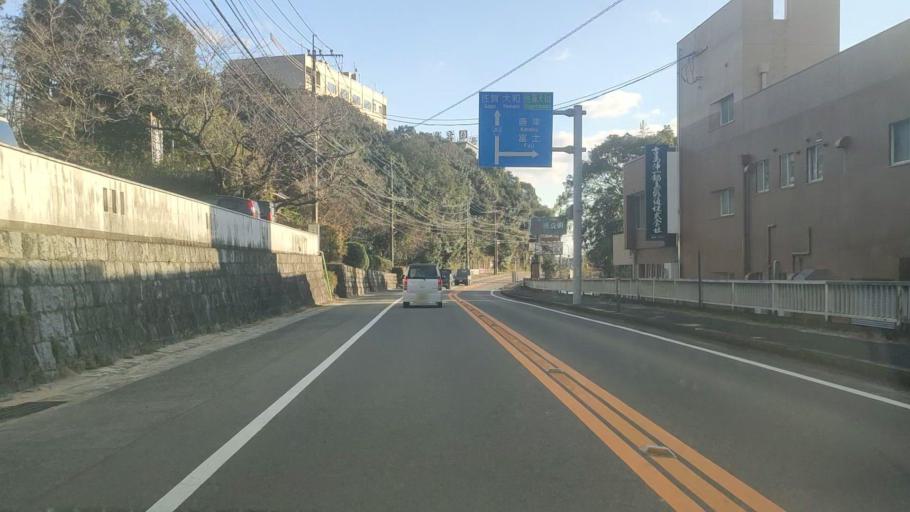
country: JP
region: Saga Prefecture
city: Saga-shi
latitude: 33.3288
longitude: 130.2686
